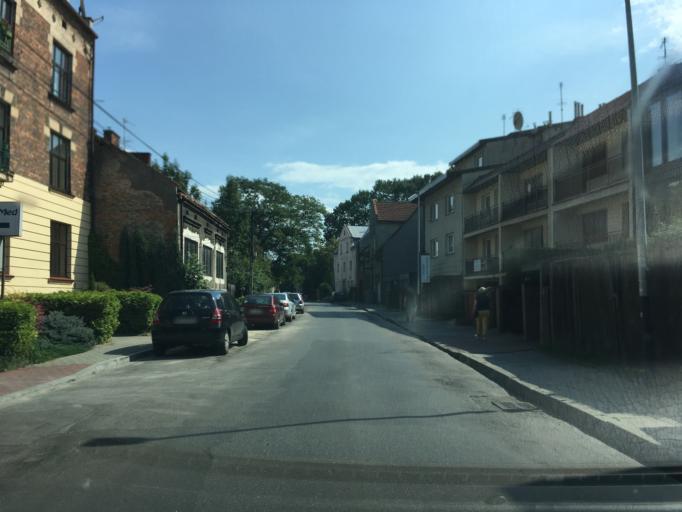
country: PL
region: Lesser Poland Voivodeship
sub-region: Krakow
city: Krakow
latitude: 50.0552
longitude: 19.9076
